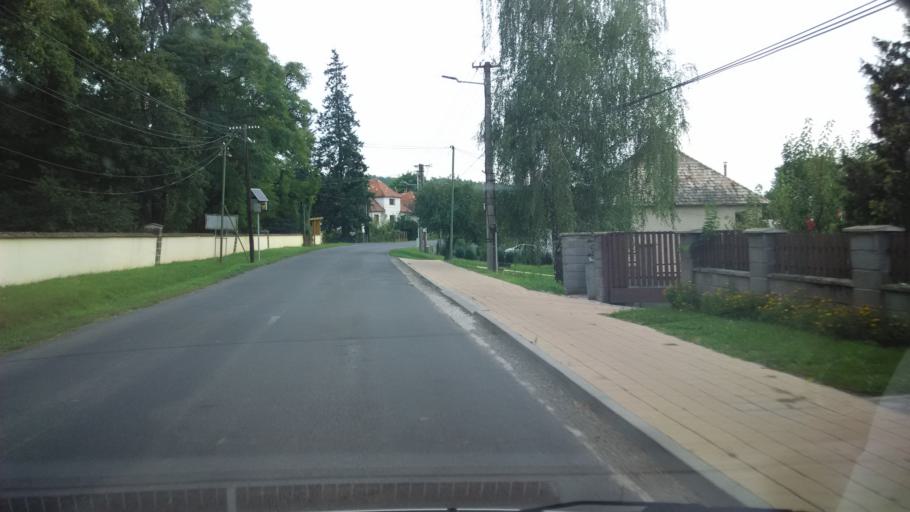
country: SK
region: Banskobystricky
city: Dudince
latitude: 48.1858
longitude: 18.8518
